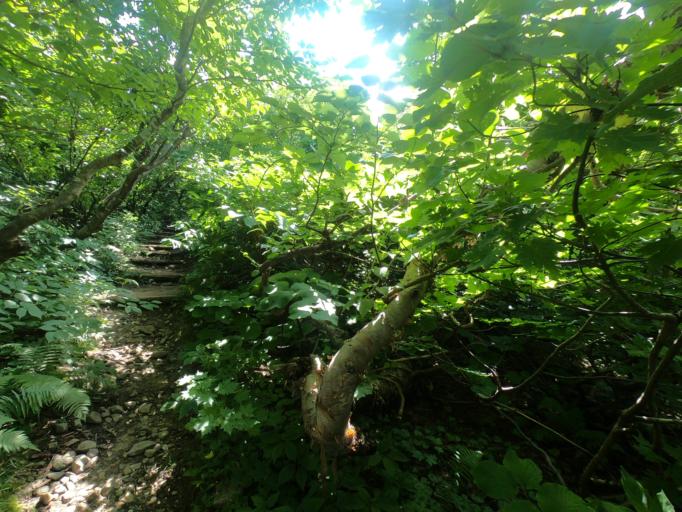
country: JP
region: Akita
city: Yuzawa
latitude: 38.9747
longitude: 140.7771
